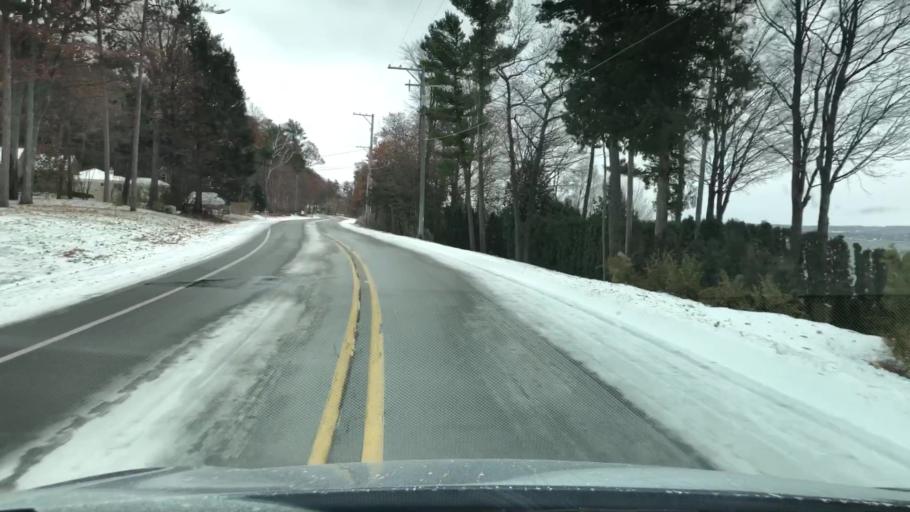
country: US
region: Michigan
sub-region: Grand Traverse County
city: Traverse City
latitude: 44.7921
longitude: -85.5867
